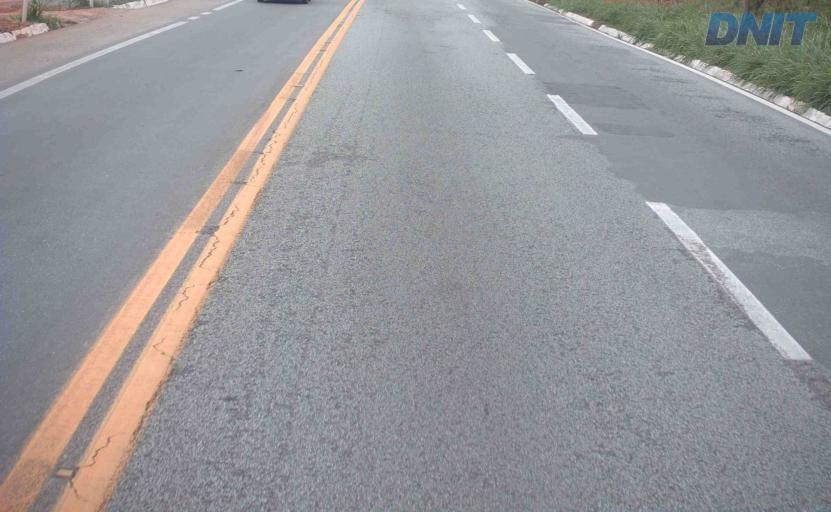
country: BR
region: Minas Gerais
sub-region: Caete
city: Caete
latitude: -19.7459
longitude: -43.5213
